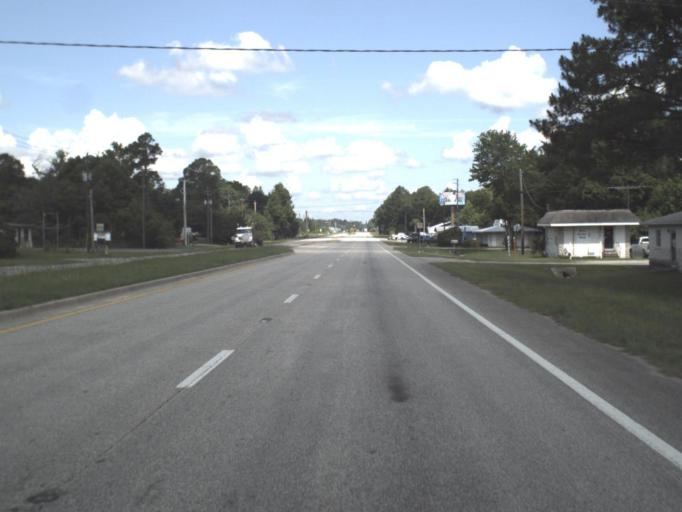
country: US
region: Florida
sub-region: Putnam County
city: Palatka
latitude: 29.6604
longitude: -81.6748
